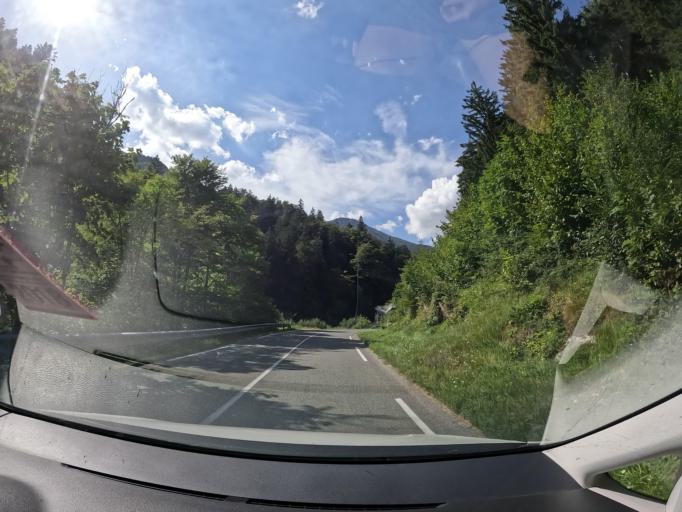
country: SI
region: Jezersko
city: Zgornje Jezersko
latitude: 46.3622
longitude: 14.4513
